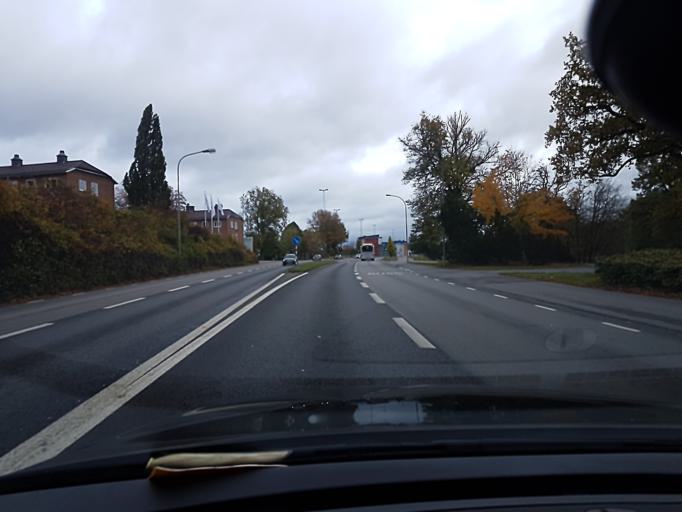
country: SE
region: Kronoberg
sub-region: Vaxjo Kommun
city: Vaexjoe
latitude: 56.8742
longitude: 14.8171
